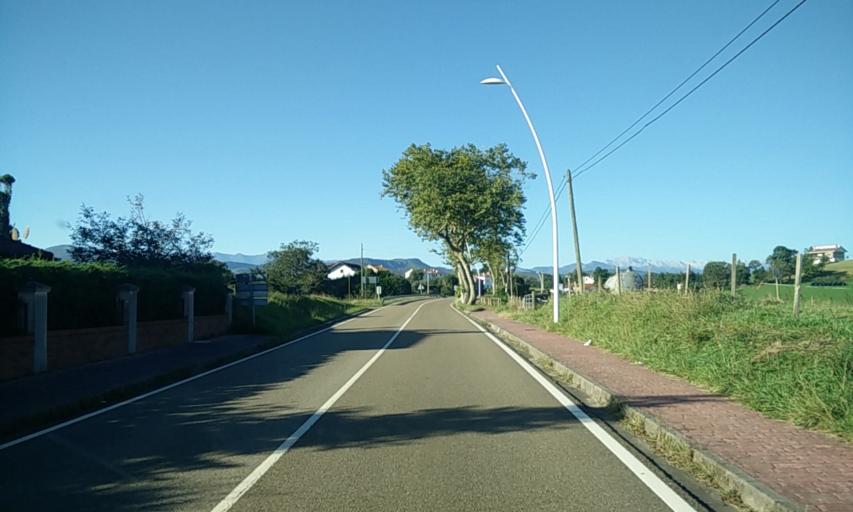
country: ES
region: Cantabria
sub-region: Provincia de Cantabria
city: San Vicente de la Barquera
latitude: 43.3761
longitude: -4.3643
